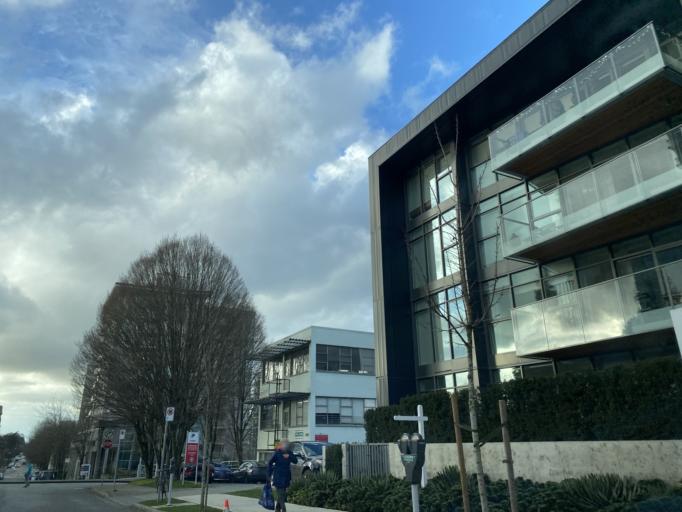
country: CA
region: British Columbia
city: West End
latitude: 49.2645
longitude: -123.1401
